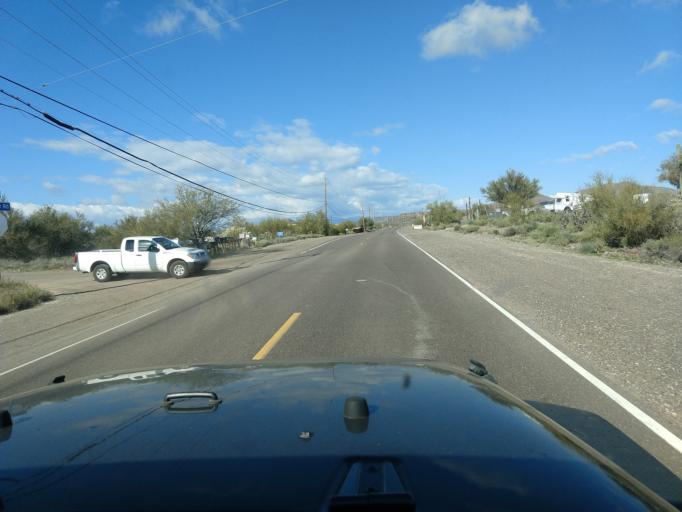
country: US
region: Arizona
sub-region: Maricopa County
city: New River
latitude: 33.9114
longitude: -112.0863
